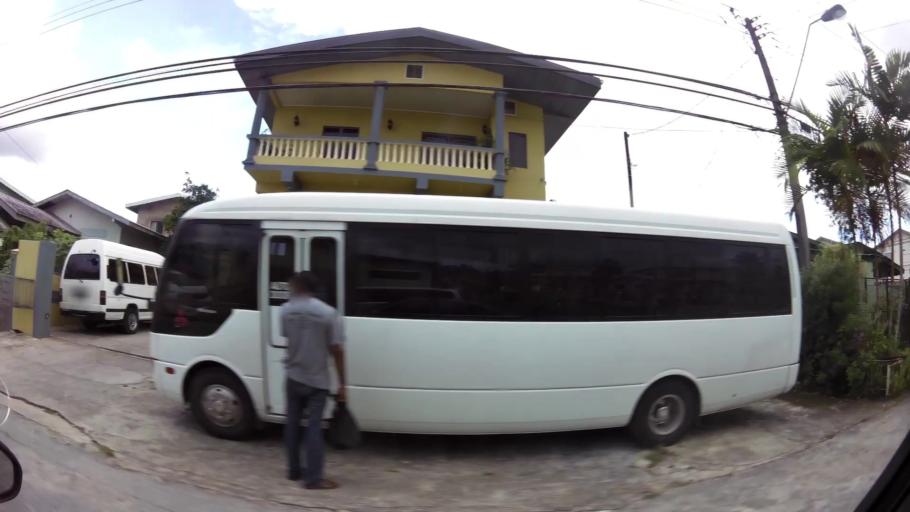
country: TT
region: City of San Fernando
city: Mon Repos
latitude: 10.2520
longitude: -61.4564
